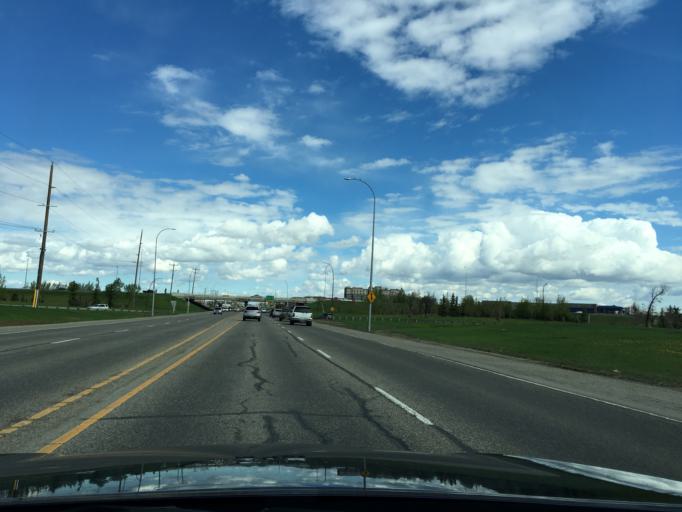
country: CA
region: Alberta
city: Calgary
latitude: 51.0643
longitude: -114.0017
